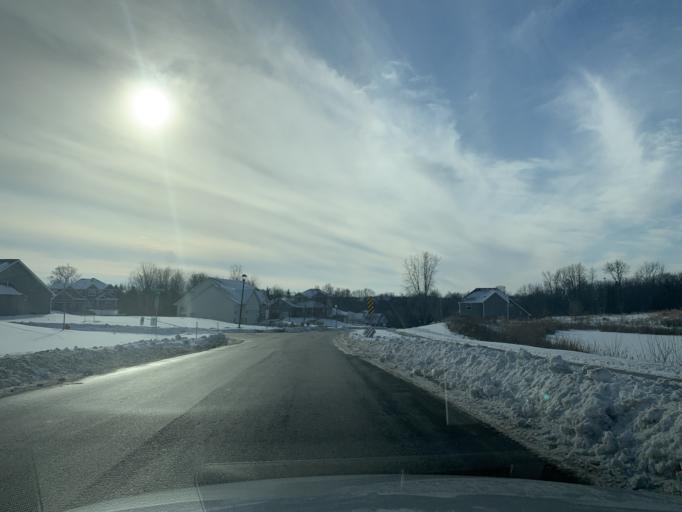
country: US
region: Minnesota
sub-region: Wright County
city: Saint Michael
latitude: 45.2067
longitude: -93.6591
